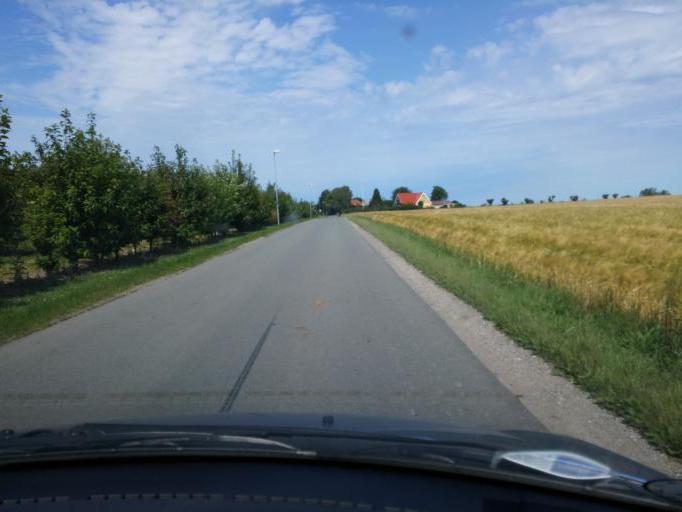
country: DK
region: South Denmark
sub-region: Kerteminde Kommune
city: Langeskov
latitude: 55.4021
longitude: 10.6098
